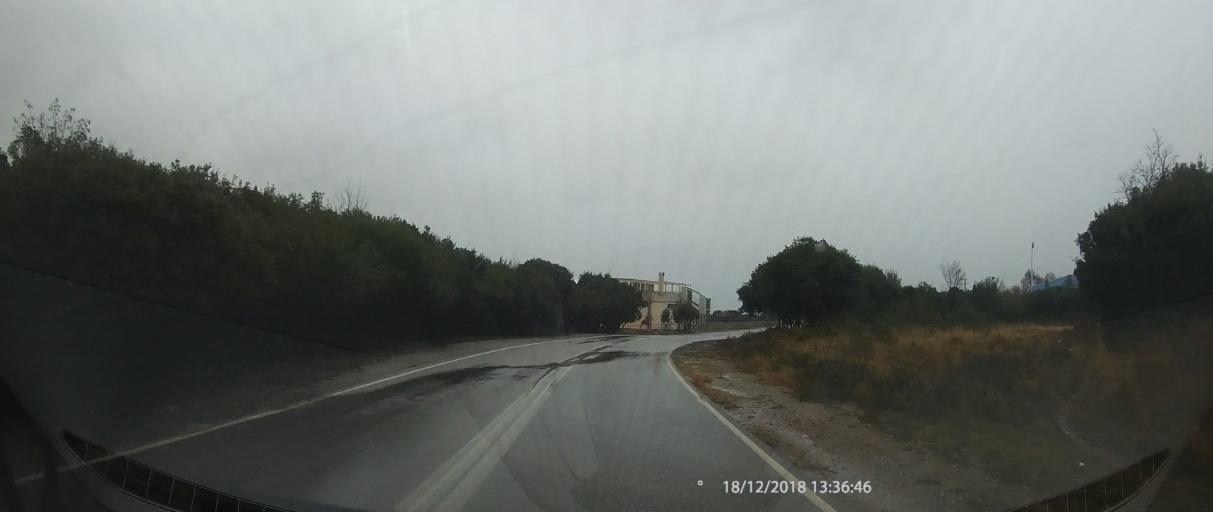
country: GR
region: Central Macedonia
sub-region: Nomos Pierias
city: Litochoro
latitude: 40.1104
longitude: 22.4974
